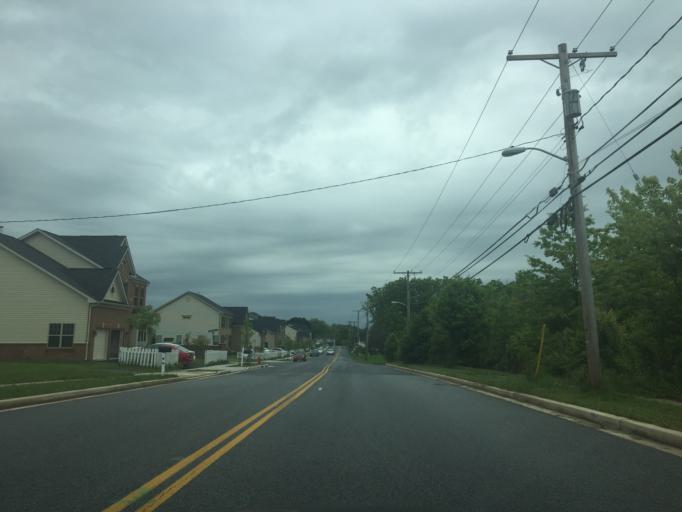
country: US
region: Maryland
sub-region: Baltimore County
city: Perry Hall
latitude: 39.4086
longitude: -76.4515
